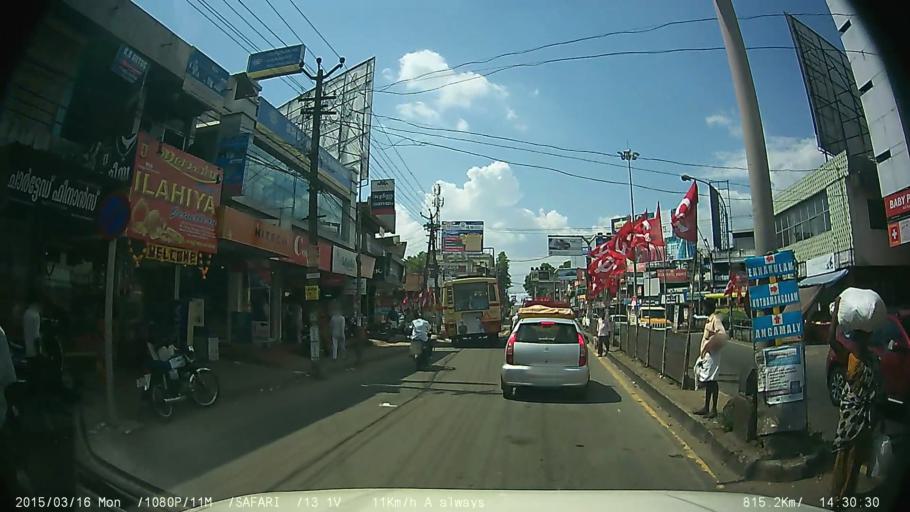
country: IN
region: Kerala
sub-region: Ernakulam
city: Perumpavur
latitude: 10.1142
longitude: 76.4780
